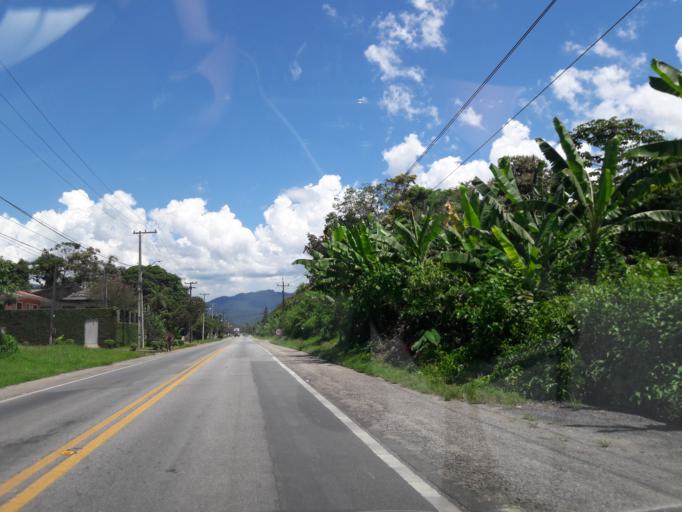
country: BR
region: Parana
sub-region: Antonina
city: Antonina
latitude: -25.4651
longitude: -48.8253
